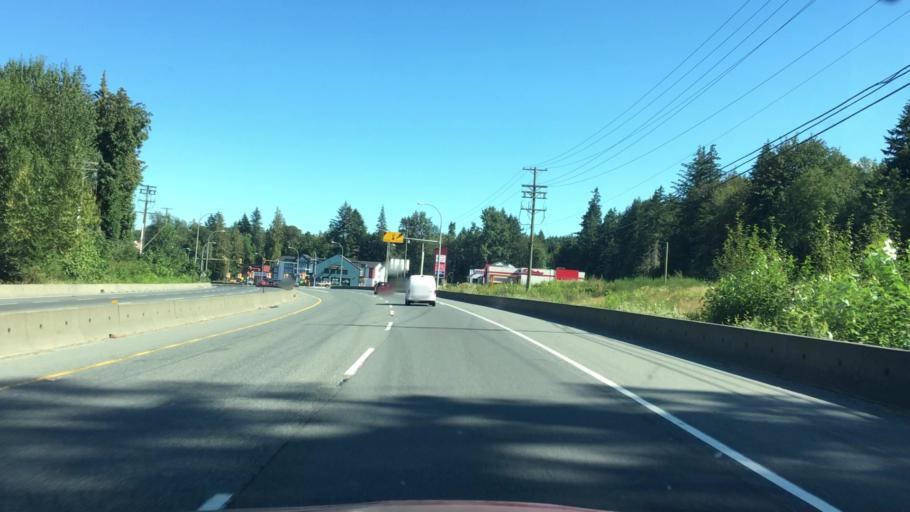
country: CA
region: British Columbia
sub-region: Cowichan Valley Regional District
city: Ladysmith
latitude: 49.0167
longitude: -123.8569
